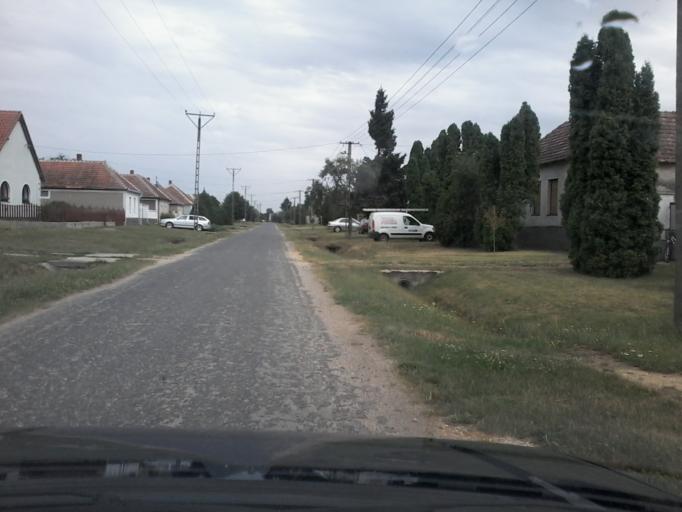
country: HU
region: Vas
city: Celldomolk
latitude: 47.2108
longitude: 17.0581
